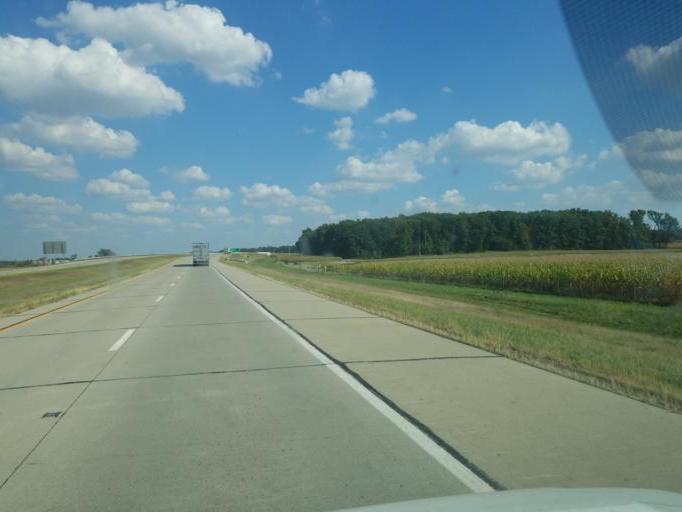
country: US
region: Ohio
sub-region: Allen County
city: Bluffton
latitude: 40.8289
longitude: -83.9433
